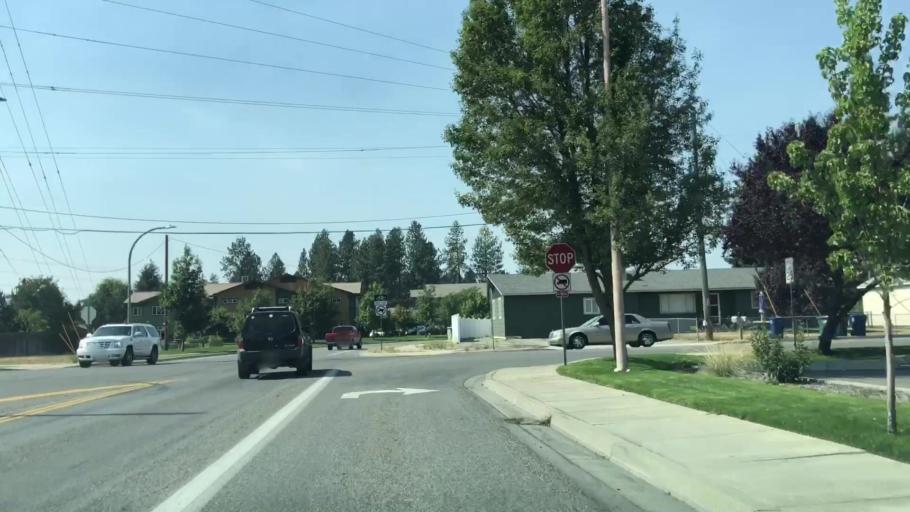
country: US
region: Idaho
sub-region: Kootenai County
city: Coeur d'Alene
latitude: 47.7072
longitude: -116.7940
